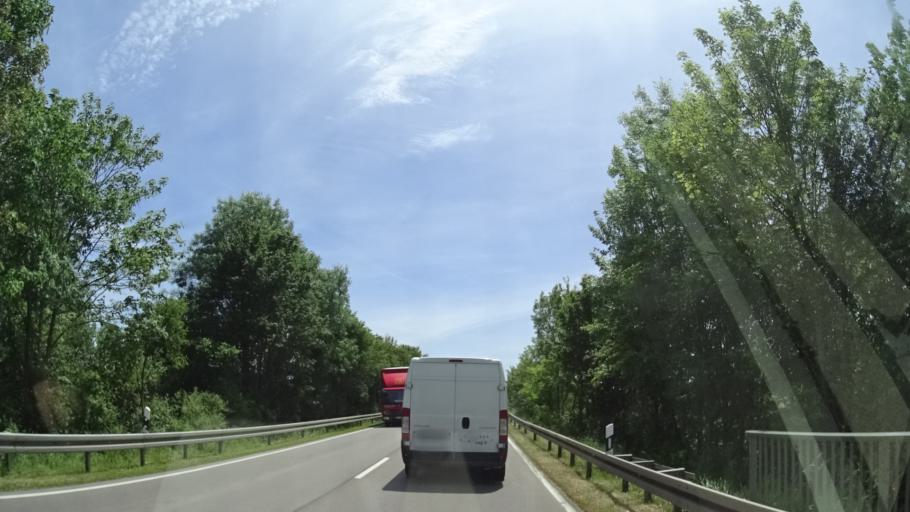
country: DE
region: Baden-Wuerttemberg
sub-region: Regierungsbezirk Stuttgart
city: Untermunkheim
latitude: 49.1726
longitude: 9.7128
